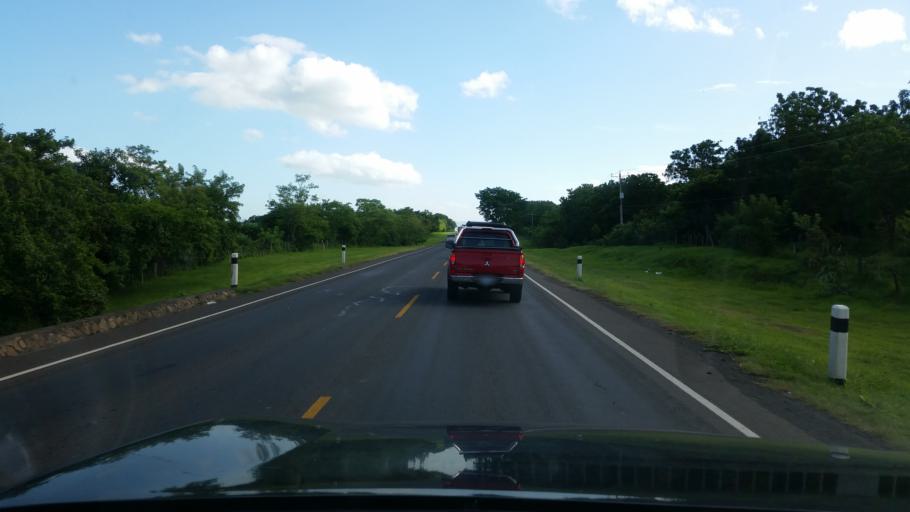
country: NI
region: Managua
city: Tipitapa
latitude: 12.3366
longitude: -86.0513
